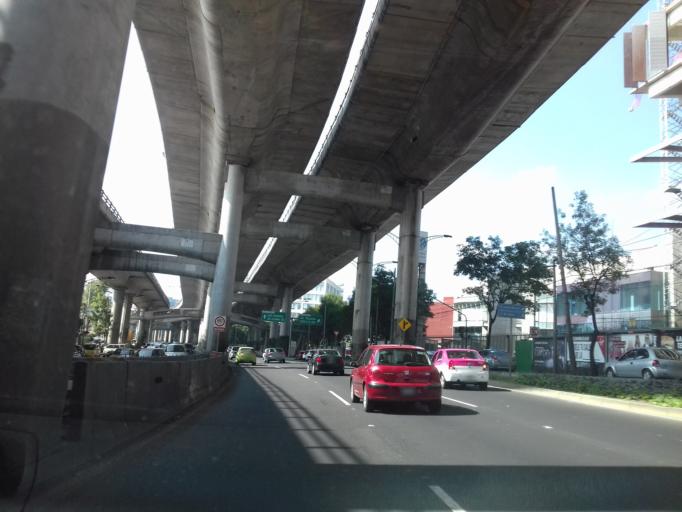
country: MX
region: Mexico City
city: Alvaro Obregon
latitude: 19.3550
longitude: -99.1998
